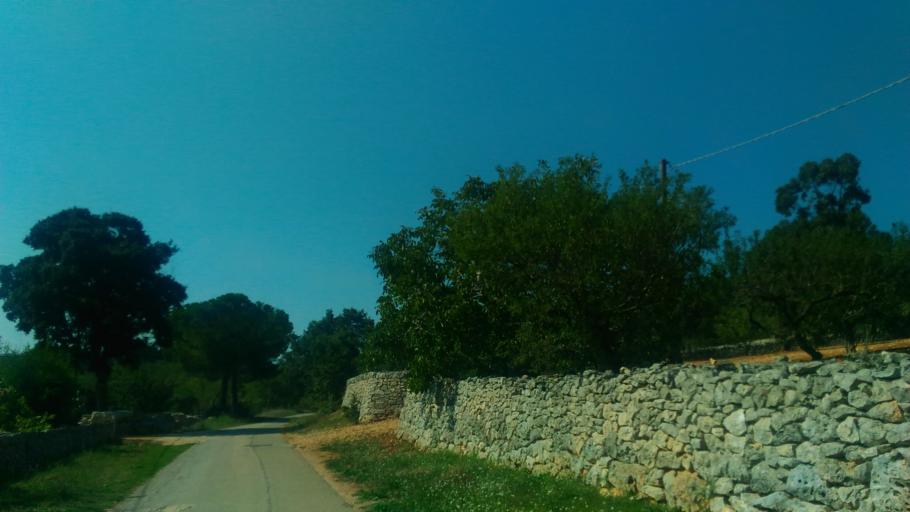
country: IT
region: Apulia
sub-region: Provincia di Bari
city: Noci
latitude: 40.8205
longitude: 17.1745
